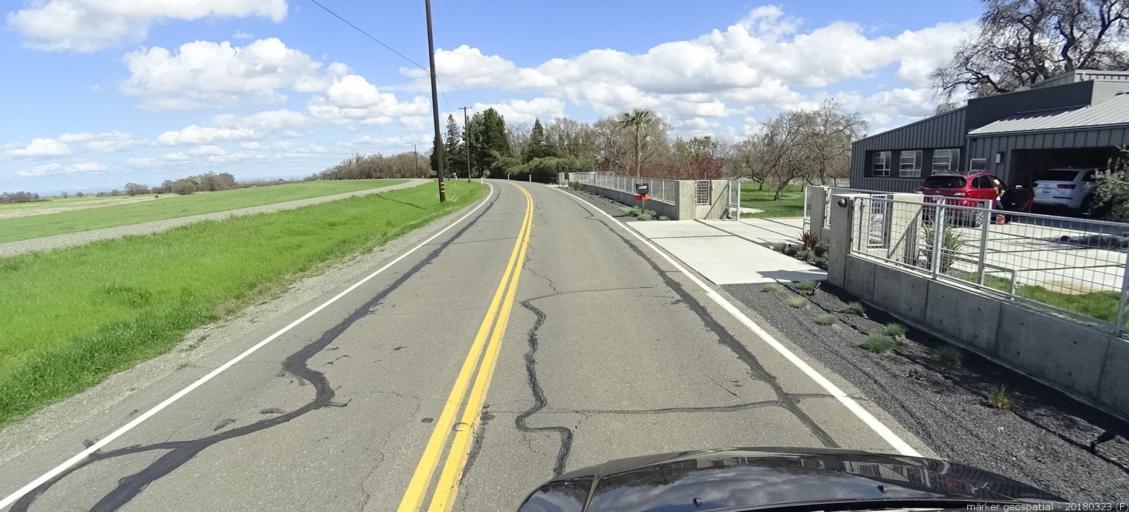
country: US
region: California
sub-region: Yolo County
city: West Sacramento
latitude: 38.6442
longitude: -121.5888
